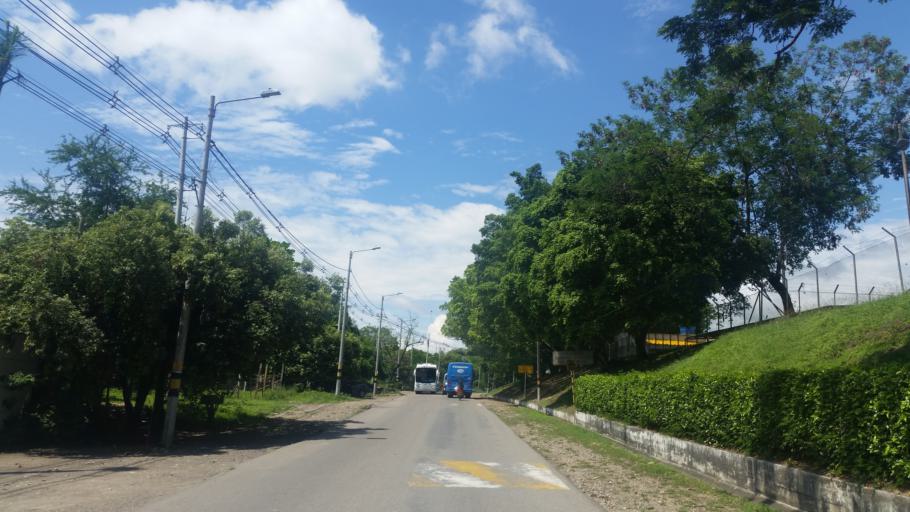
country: CO
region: Huila
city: Neiva
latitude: 2.9866
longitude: -75.2749
